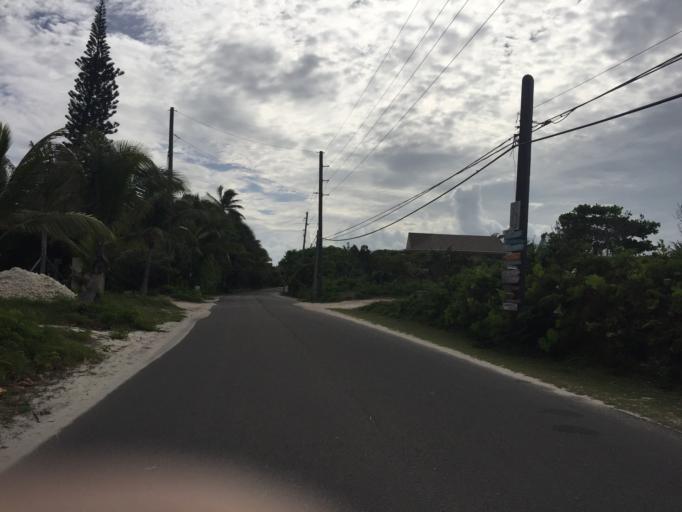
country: BS
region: Central Abaco
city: Marsh Harbour
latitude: 26.5283
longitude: -76.9631
